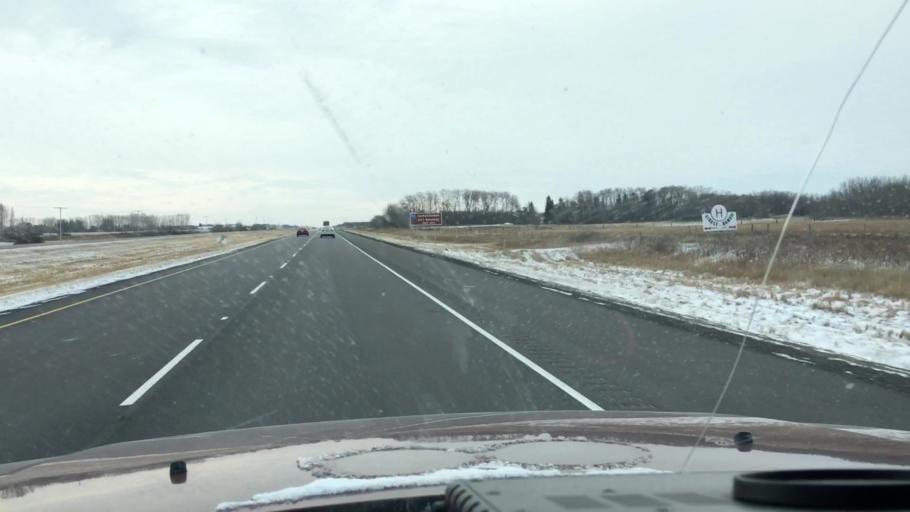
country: CA
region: Saskatchewan
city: Saskatoon
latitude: 51.9785
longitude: -106.5580
